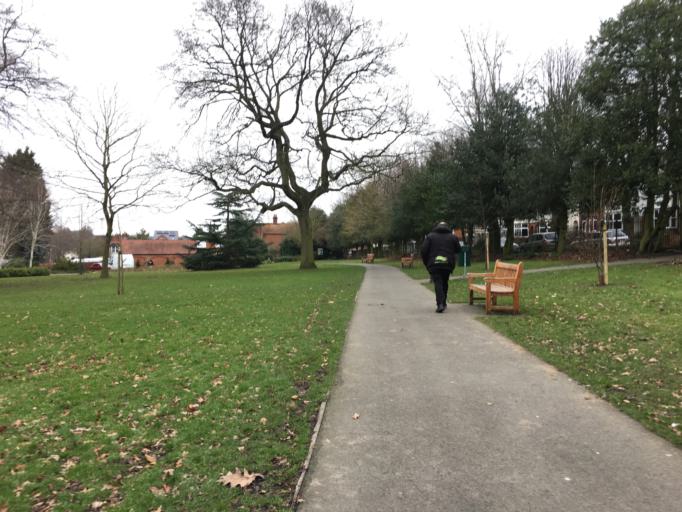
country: GB
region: England
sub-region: Warwickshire
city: Rugby
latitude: 52.3765
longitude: -1.2618
